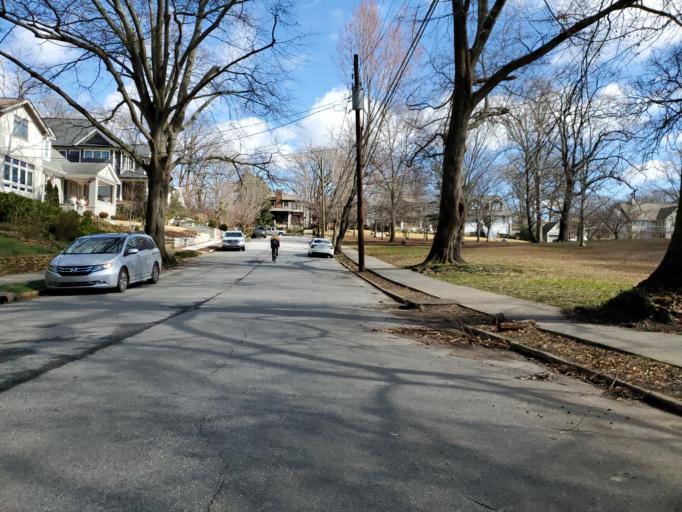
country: US
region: Georgia
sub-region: DeKalb County
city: Druid Hills
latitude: 33.7830
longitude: -84.3606
